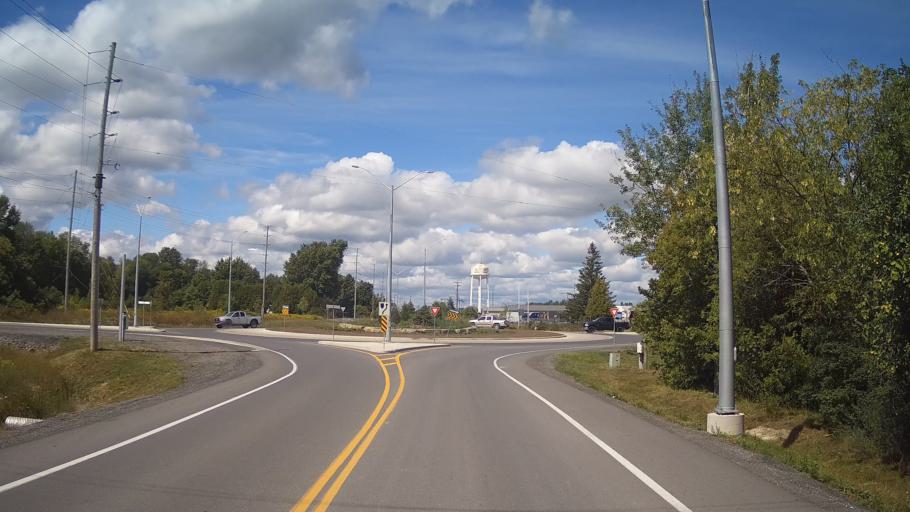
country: US
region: New York
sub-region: St. Lawrence County
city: Ogdensburg
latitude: 44.8462
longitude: -75.3218
